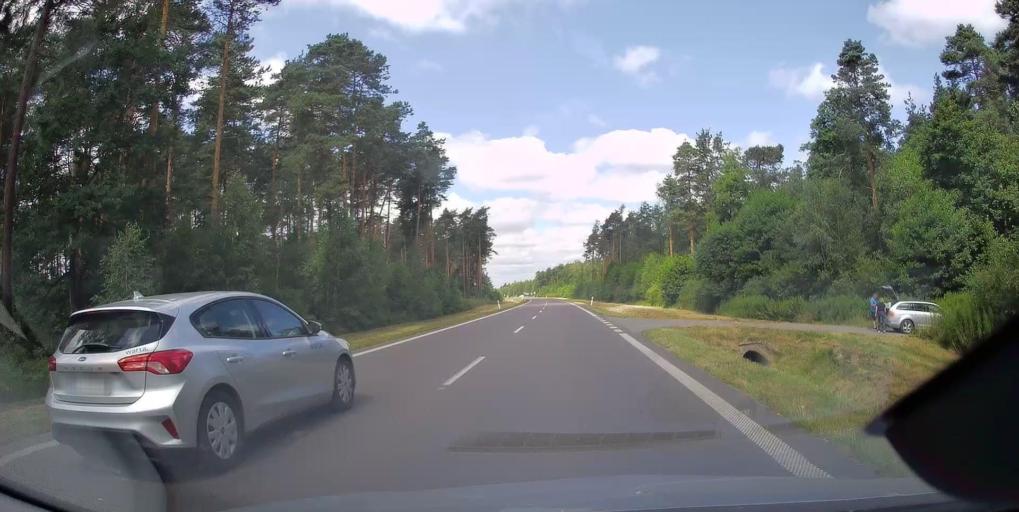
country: PL
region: Subcarpathian Voivodeship
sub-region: Powiat mielecki
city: Mielec
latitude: 50.3204
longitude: 21.4974
